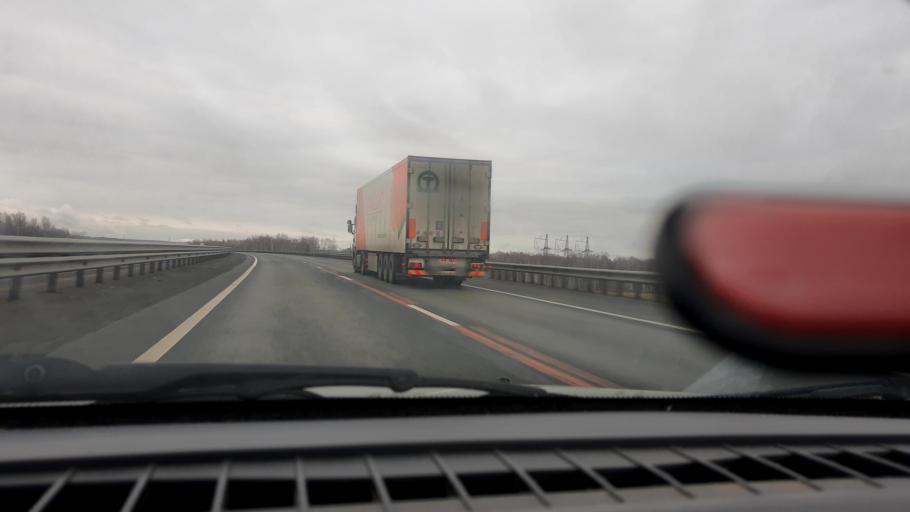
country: RU
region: Nizjnij Novgorod
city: Burevestnik
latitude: 56.1150
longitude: 43.8289
